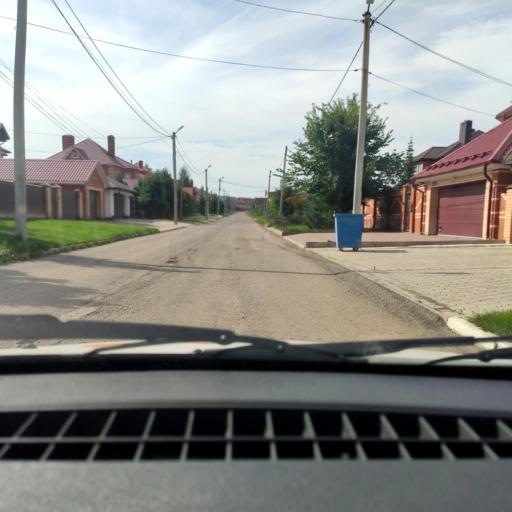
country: RU
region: Bashkortostan
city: Kabakovo
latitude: 54.6248
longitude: 56.1290
